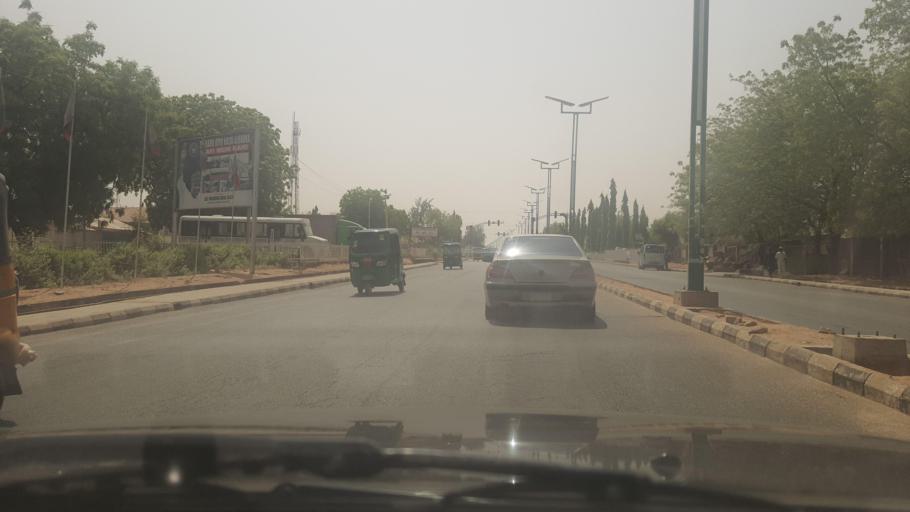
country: NG
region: Gombe
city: Gombe
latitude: 10.2844
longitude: 11.1486
